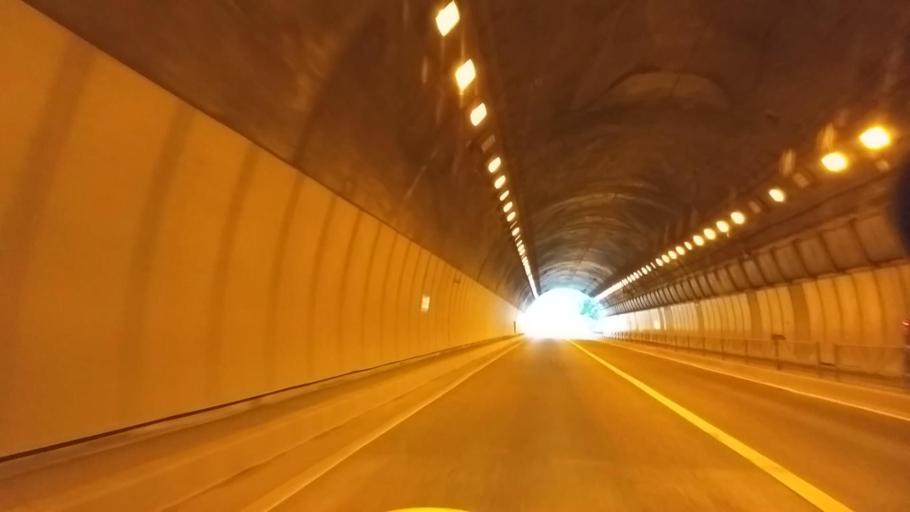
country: JP
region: Shizuoka
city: Fujinomiya
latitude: 35.2814
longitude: 138.4487
